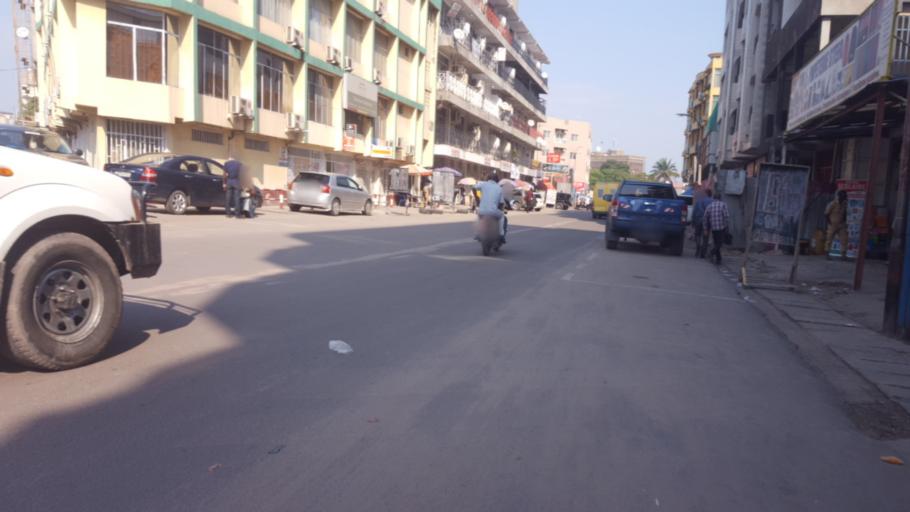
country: CD
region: Kinshasa
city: Kinshasa
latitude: -4.3056
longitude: 15.3062
